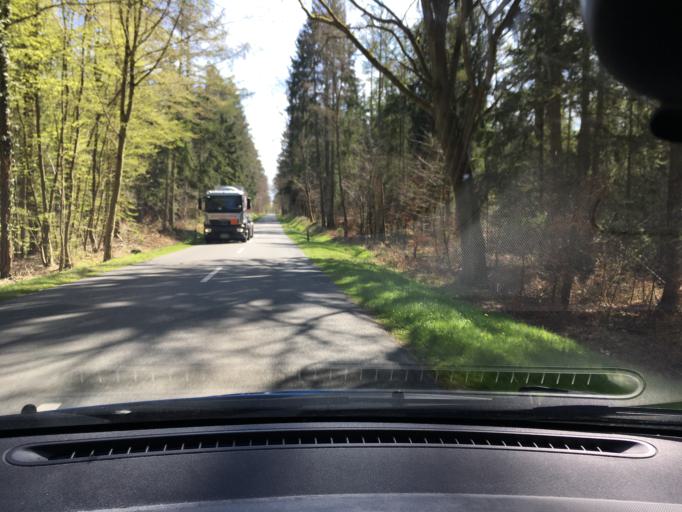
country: DE
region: Lower Saxony
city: Romstedt
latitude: 53.1364
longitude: 10.6866
